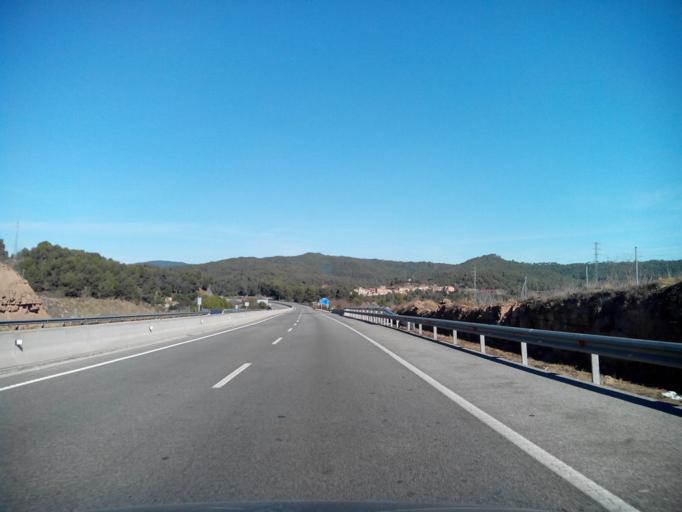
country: ES
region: Catalonia
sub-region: Provincia de Barcelona
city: Navas
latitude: 41.9057
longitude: 1.8765
